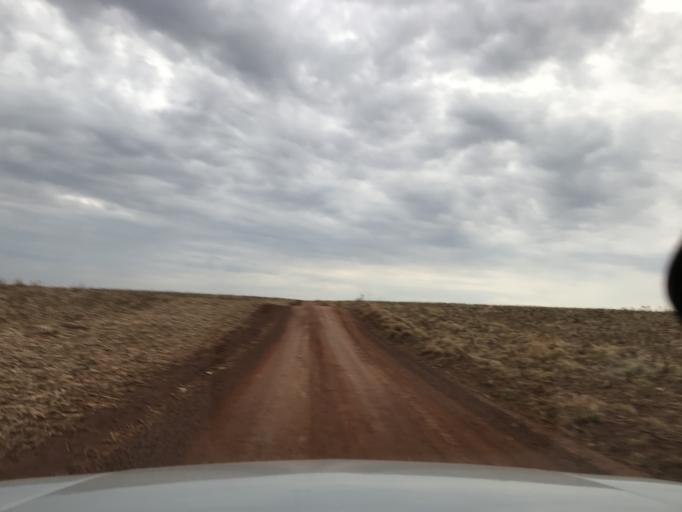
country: BR
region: Parana
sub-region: Palotina
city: Palotina
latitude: -24.2208
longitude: -53.8352
